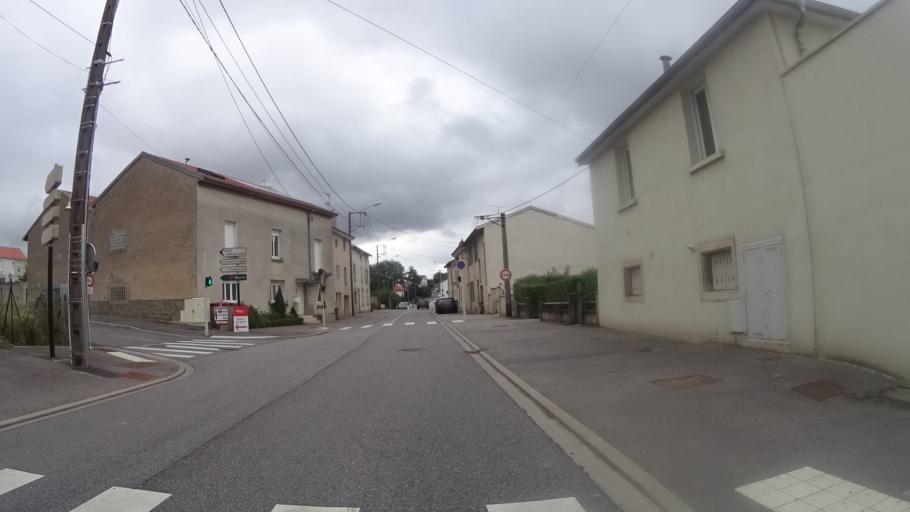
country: FR
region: Lorraine
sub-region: Departement de Meurthe-et-Moselle
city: Art-sur-Meurthe
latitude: 48.6542
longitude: 6.2660
